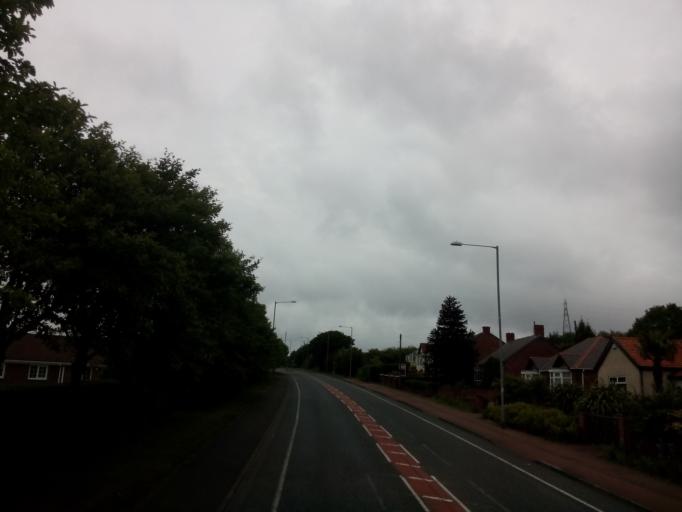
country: GB
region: England
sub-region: Gateshead
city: Lamesley
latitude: 54.9082
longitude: -1.5801
